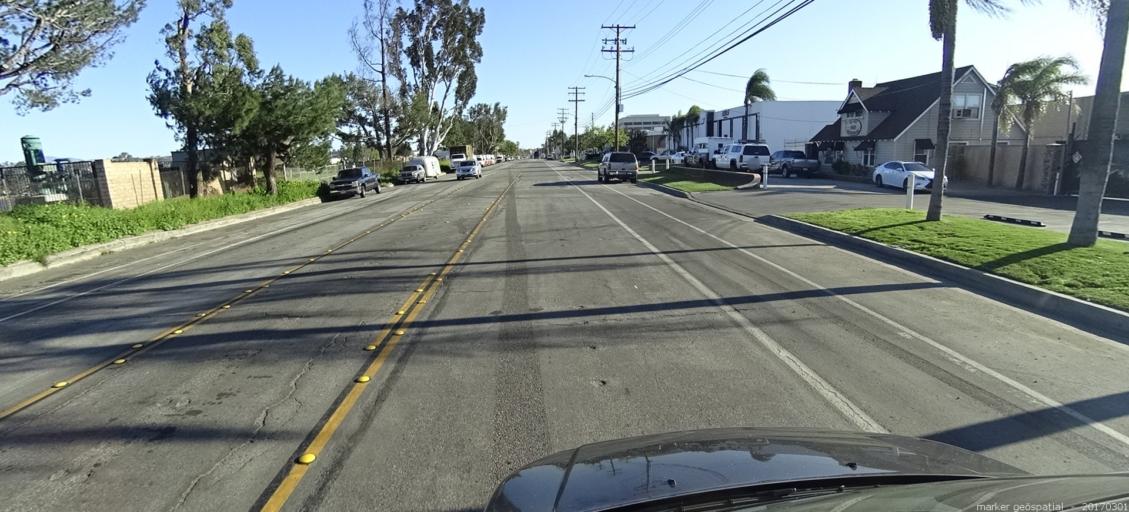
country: US
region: California
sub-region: Orange County
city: Placentia
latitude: 33.8651
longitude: -117.8511
